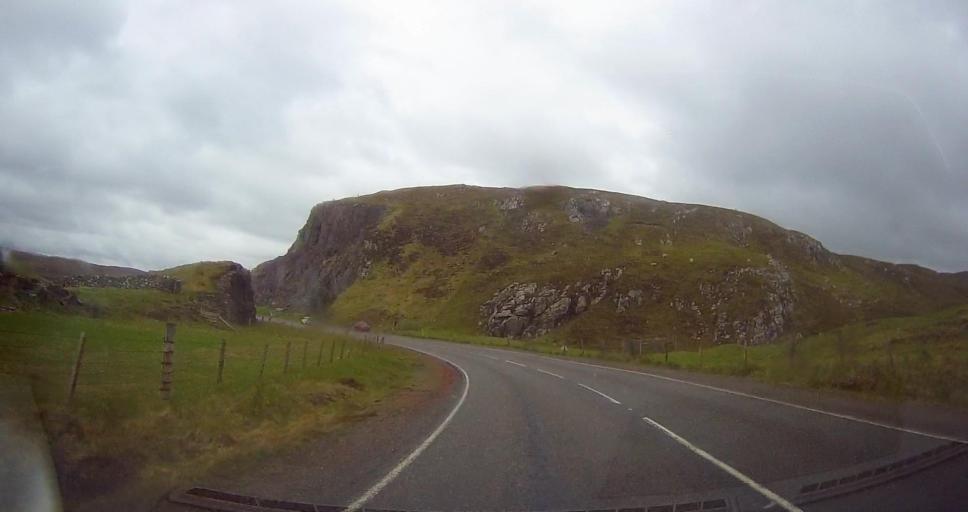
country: GB
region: Scotland
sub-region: Shetland Islands
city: Lerwick
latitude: 60.3987
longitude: -1.3852
